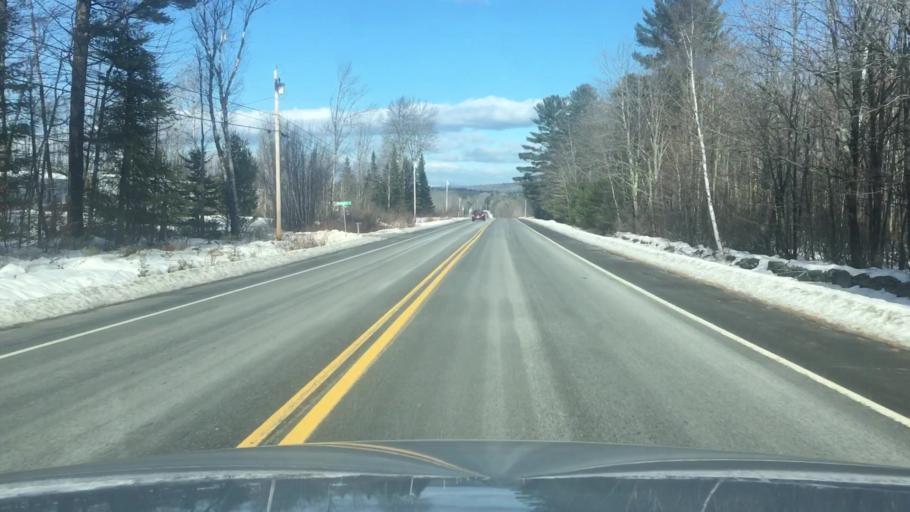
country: US
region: Maine
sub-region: Somerset County
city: Skowhegan
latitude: 44.8377
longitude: -69.7876
